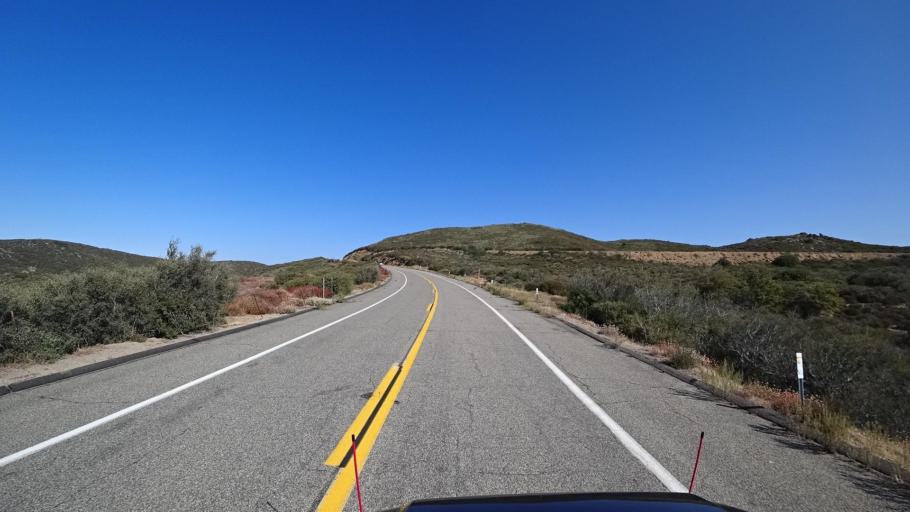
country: US
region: California
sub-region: San Diego County
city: Pine Valley
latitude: 32.9338
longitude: -116.4857
